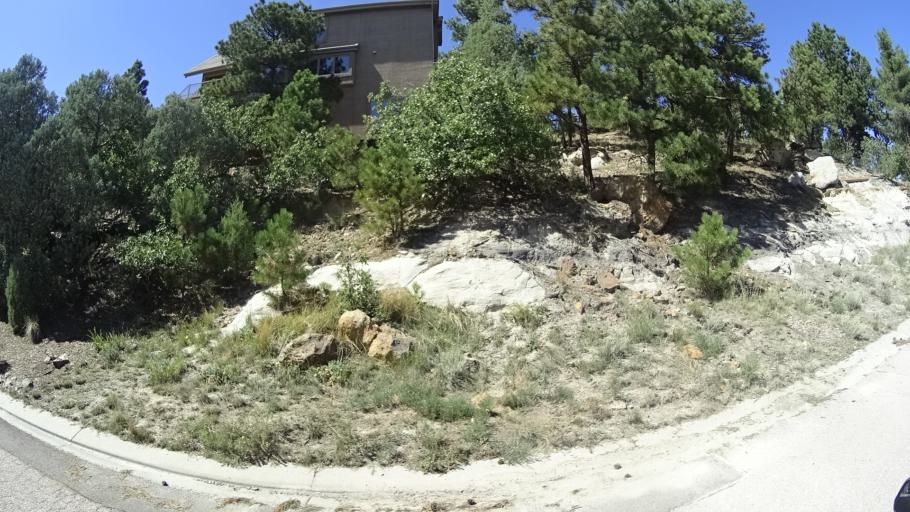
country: US
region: Colorado
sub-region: El Paso County
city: Colorado Springs
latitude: 38.9197
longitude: -104.8000
